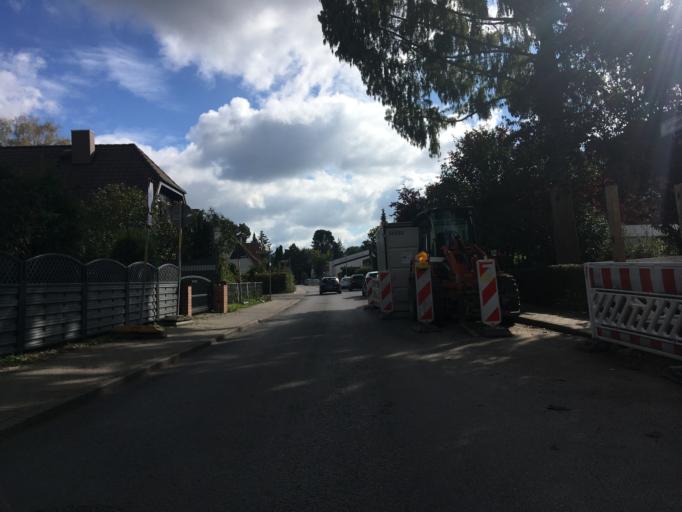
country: DE
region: Berlin
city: Rudow
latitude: 52.4098
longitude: 13.4800
